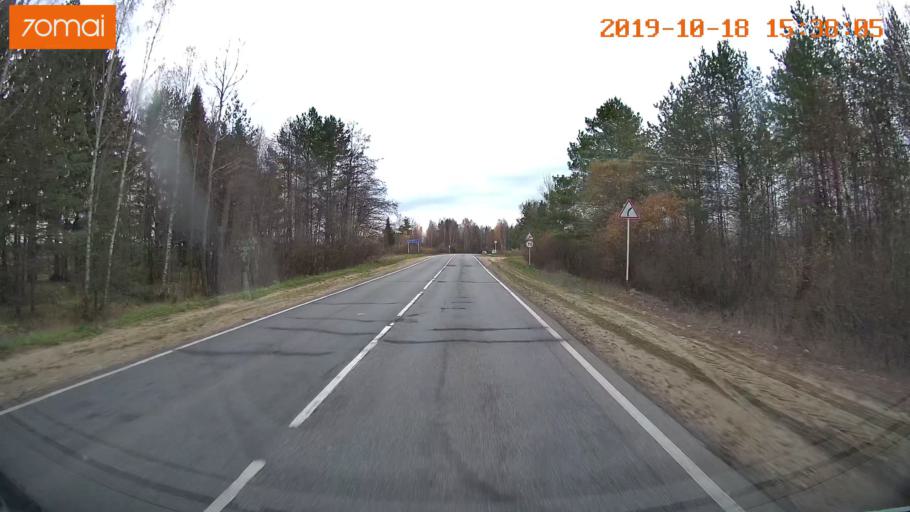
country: RU
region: Vladimir
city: Golovino
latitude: 55.9064
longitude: 40.6109
